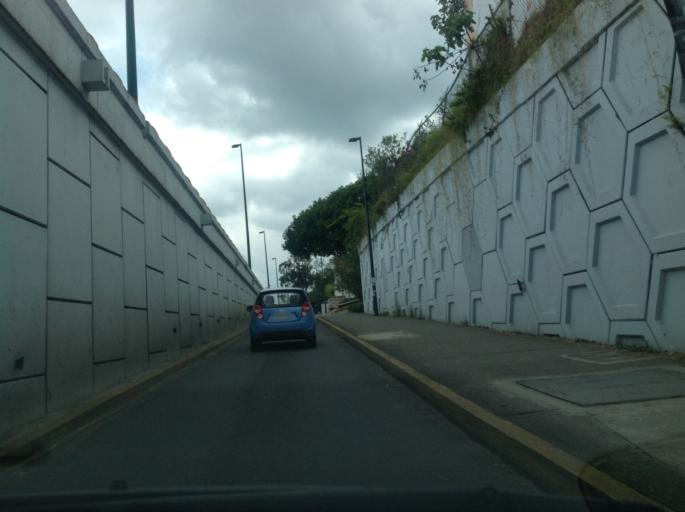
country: MX
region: Veracruz
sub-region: Xalapa
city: Xalapa de Enriquez
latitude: 19.5182
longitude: -96.9159
